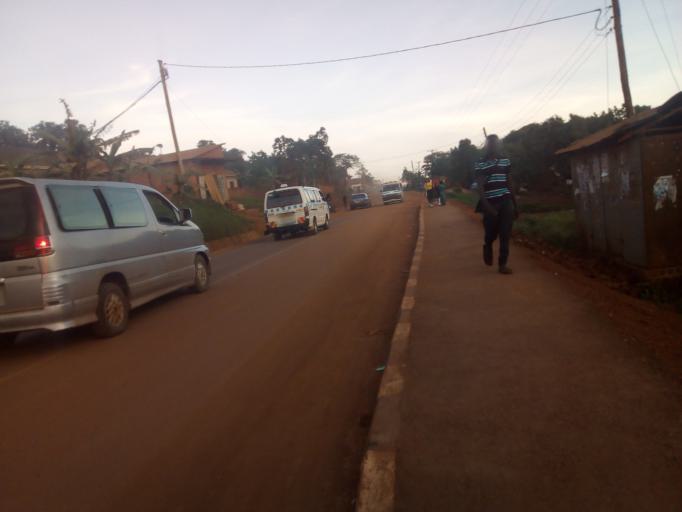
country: UG
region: Central Region
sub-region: Wakiso District
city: Kajansi
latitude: 0.2398
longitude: 32.5737
